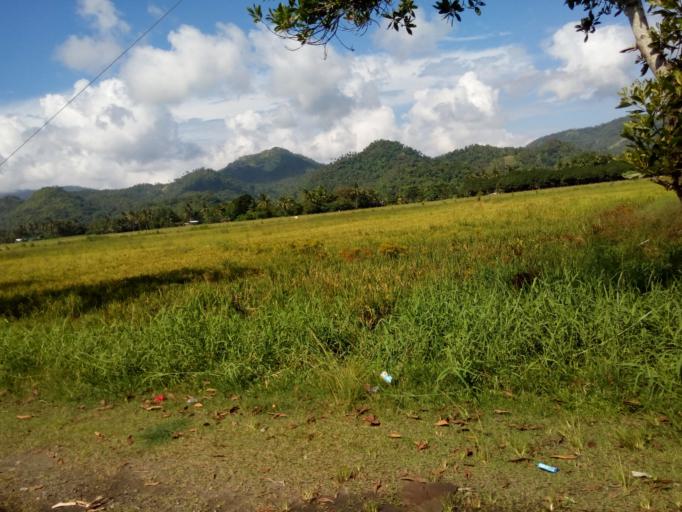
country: PH
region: Caraga
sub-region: Province of Surigao del Norte
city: Luna
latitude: 9.7578
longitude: 125.4827
